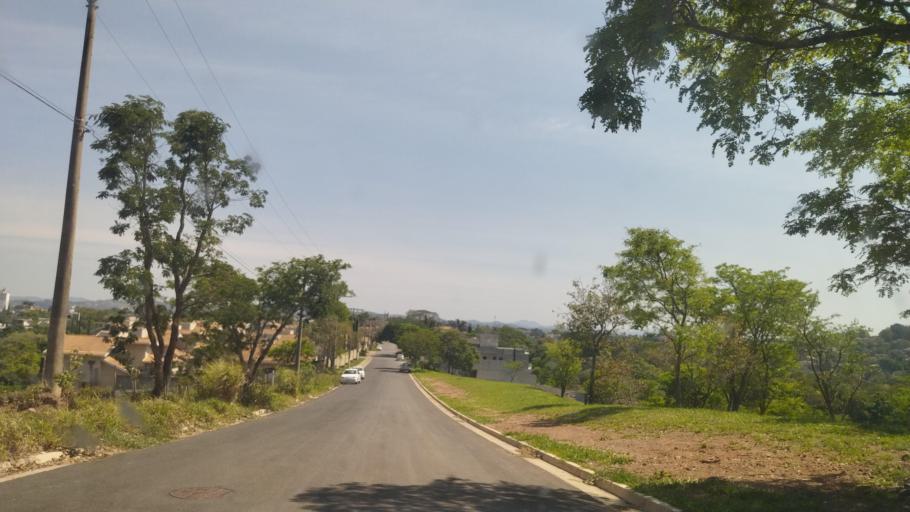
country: BR
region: Sao Paulo
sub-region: Atibaia
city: Atibaia
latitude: -23.1317
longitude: -46.5445
